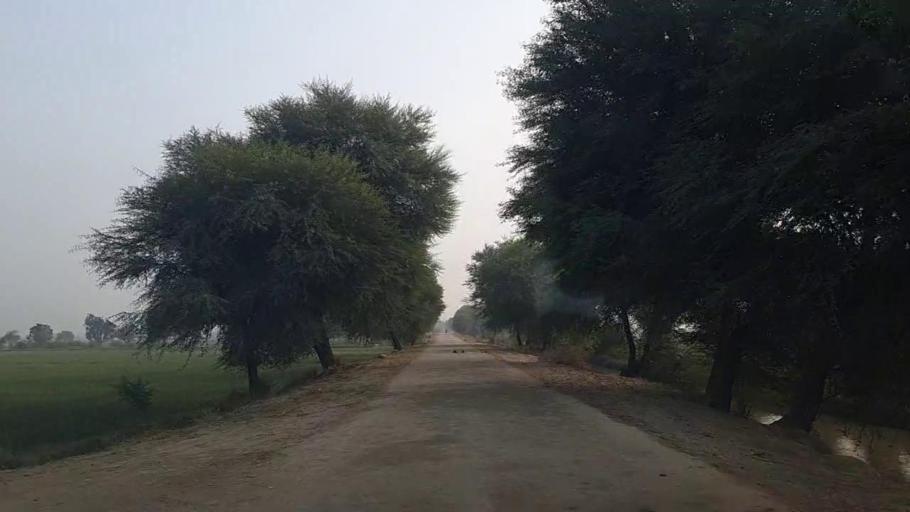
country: PK
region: Sindh
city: Sinjhoro
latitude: 26.1183
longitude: 68.8034
